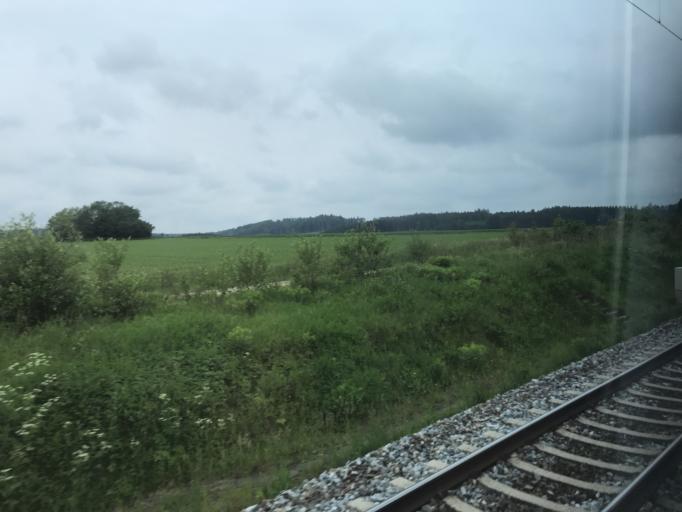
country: DE
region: Bavaria
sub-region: Swabia
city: Dinkelscherben
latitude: 48.3560
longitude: 10.5609
